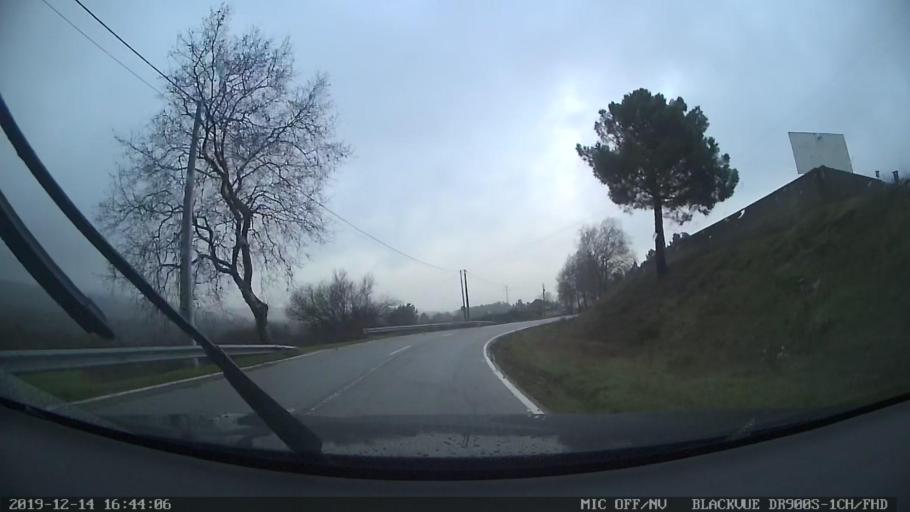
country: PT
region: Vila Real
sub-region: Murca
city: Murca
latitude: 41.3886
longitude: -7.4970
